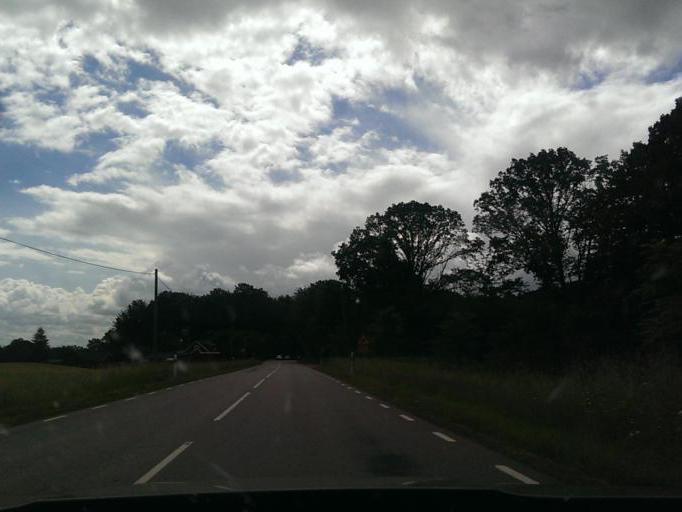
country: SE
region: Skane
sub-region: Klippans Kommun
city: Ljungbyhed
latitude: 56.0153
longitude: 13.2744
